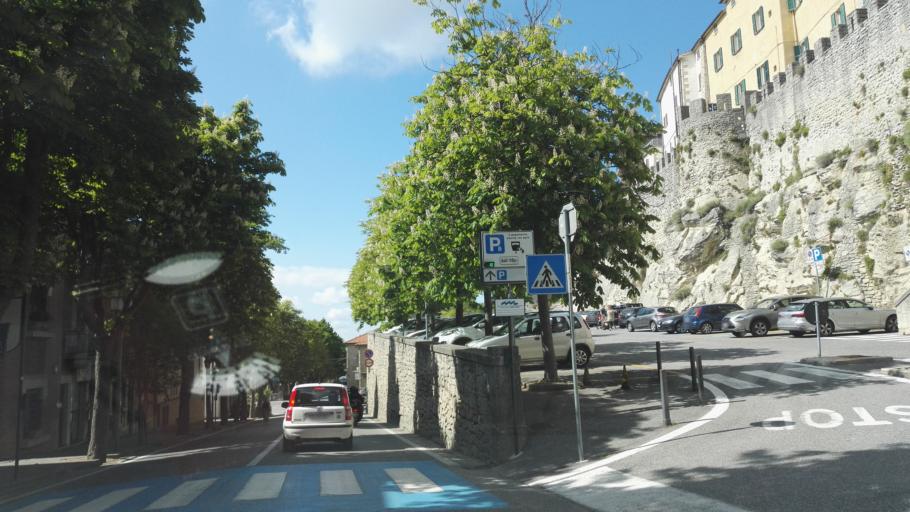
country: SM
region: San Marino
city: San Marino
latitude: 43.9370
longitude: 12.4450
